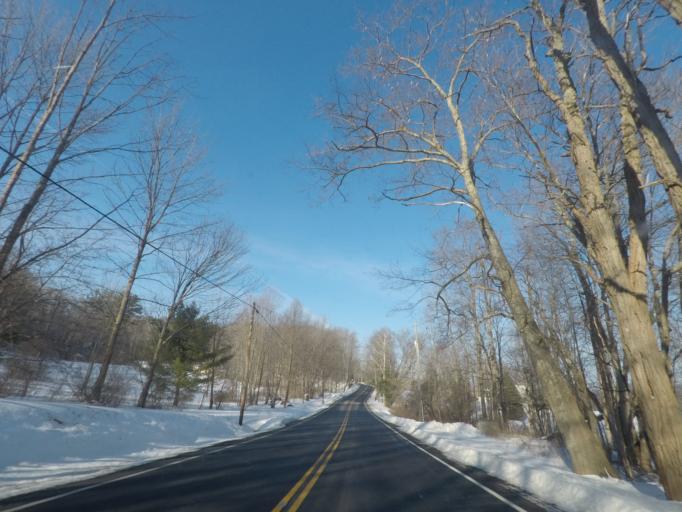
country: US
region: Massachusetts
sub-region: Berkshire County
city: Richmond
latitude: 42.5018
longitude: -73.3806
